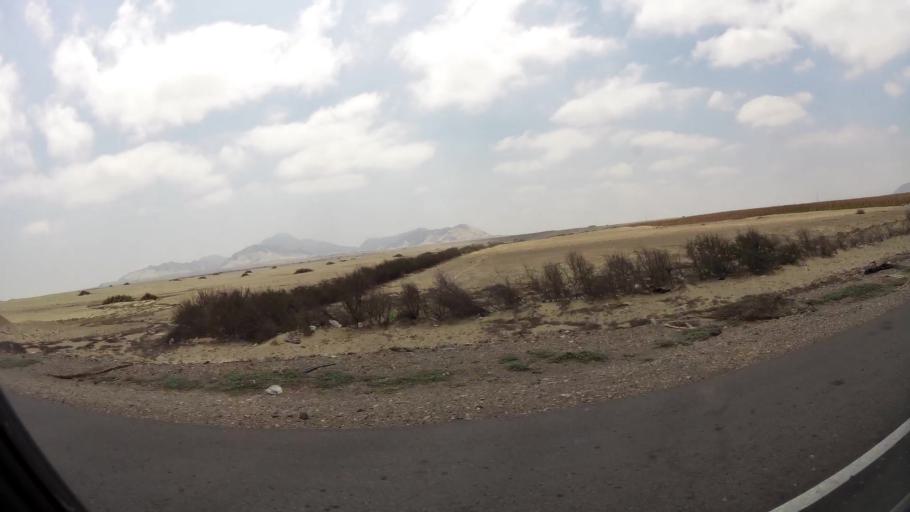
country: PE
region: La Libertad
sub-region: Ascope
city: Paijan
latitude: -7.6555
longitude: -79.3416
